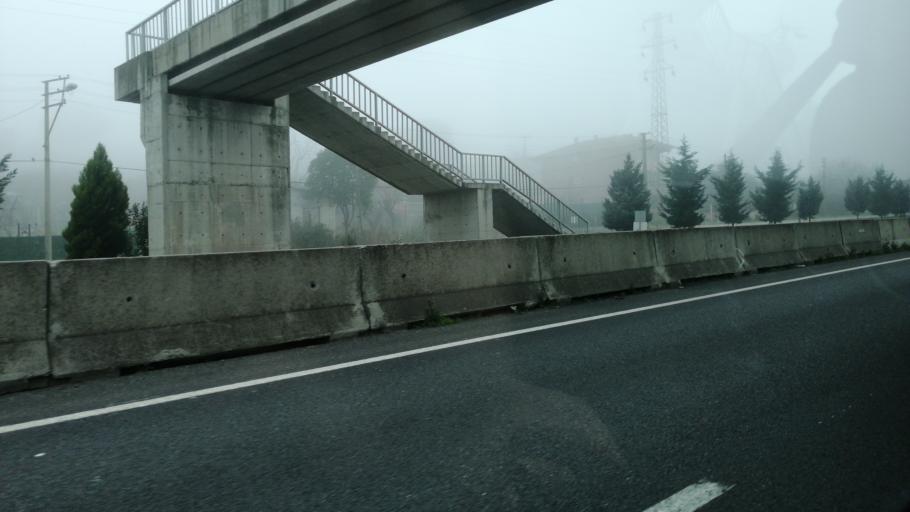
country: TR
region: Yalova
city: Ciftlikkoy
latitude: 40.6727
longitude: 29.3436
